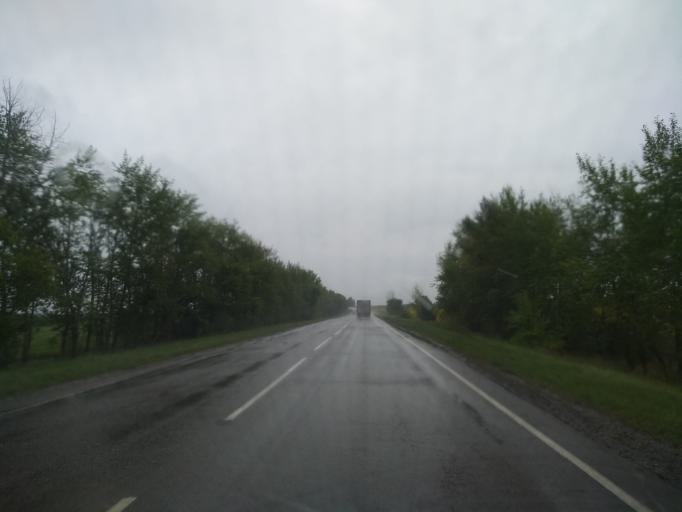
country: RU
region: Voronezj
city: Verkhnyaya Khava
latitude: 51.6907
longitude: 39.9367
